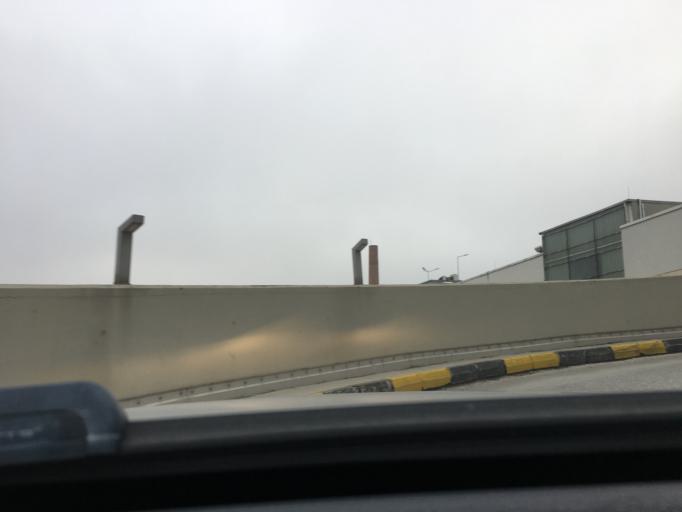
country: TR
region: Eskisehir
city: Eskisehir
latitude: 39.7828
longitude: 30.5114
